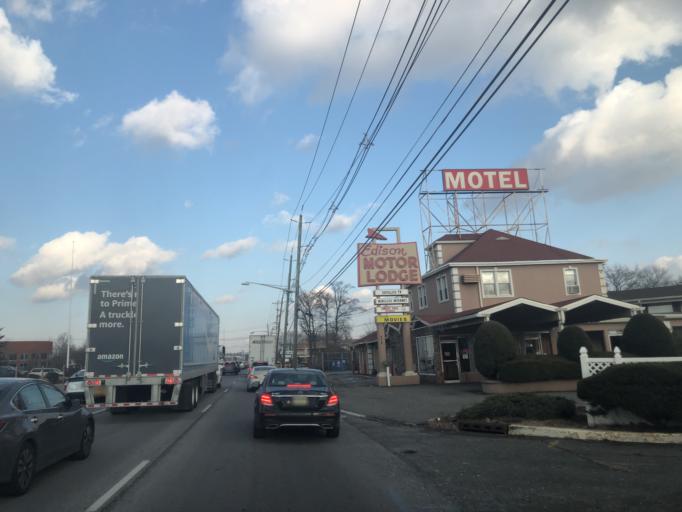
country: US
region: New Jersey
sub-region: Middlesex County
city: Piscataway
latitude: 40.5062
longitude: -74.3945
